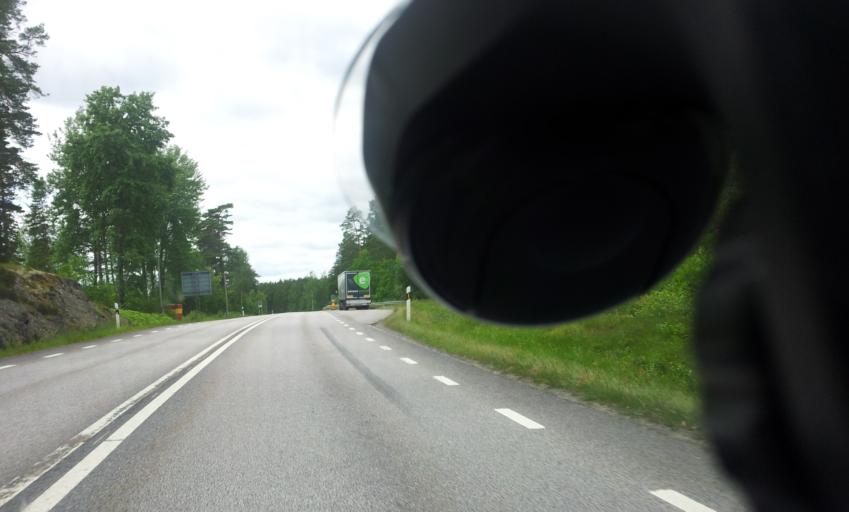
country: SE
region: Kalmar
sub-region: Vasterviks Kommun
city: Vaestervik
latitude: 57.7259
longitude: 16.5134
